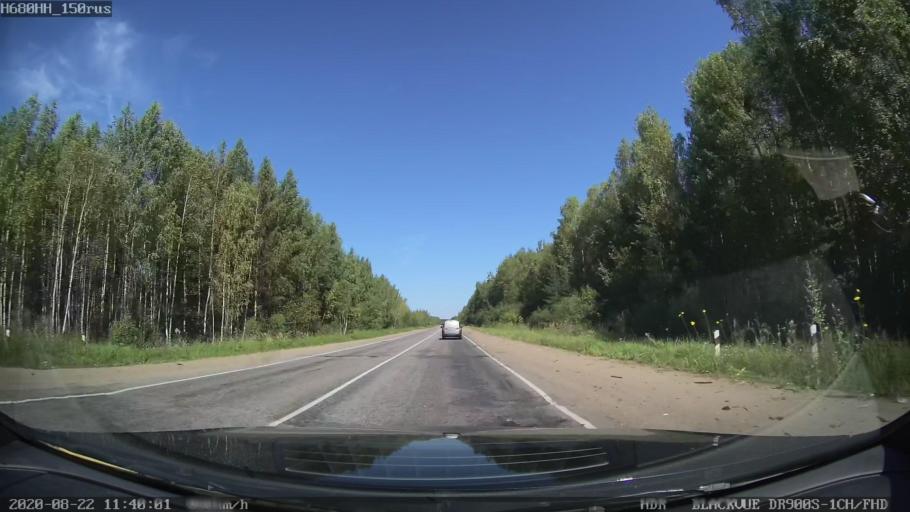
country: RU
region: Tverskaya
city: Sakharovo
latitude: 56.9718
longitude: 36.0232
